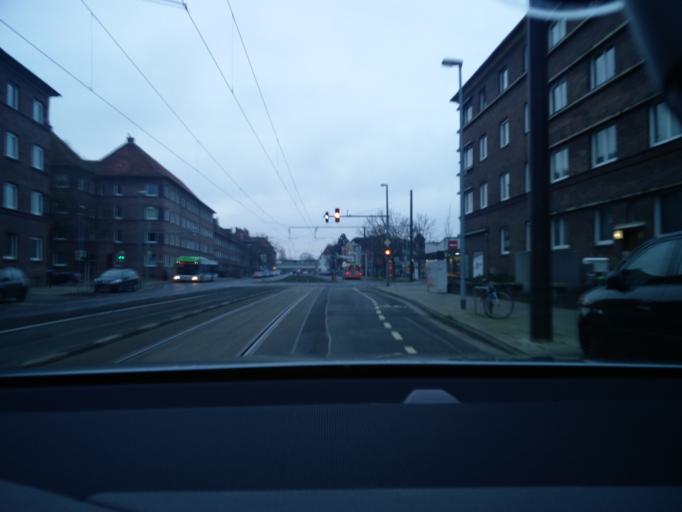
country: DE
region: Lower Saxony
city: Hannover
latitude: 52.3492
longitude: 9.7234
